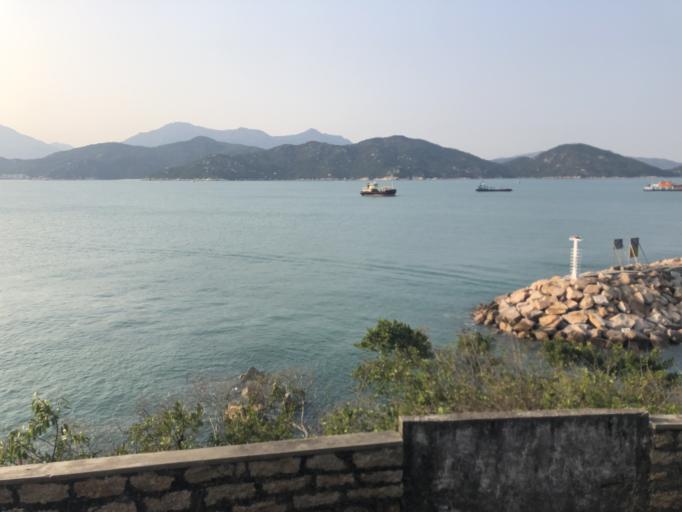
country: HK
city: Yung Shue Wan
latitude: 22.2015
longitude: 114.0185
